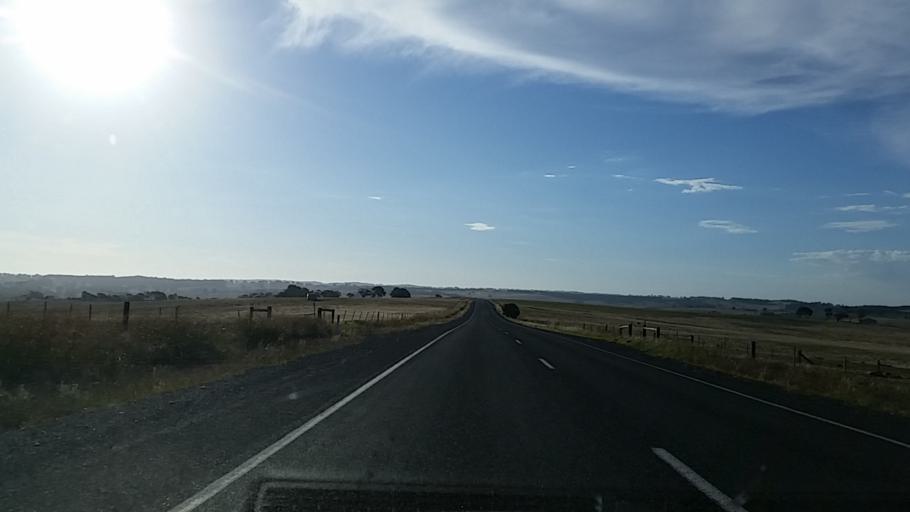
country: AU
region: South Australia
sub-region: Adelaide Hills
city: Birdwood
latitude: -34.7740
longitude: 139.1197
